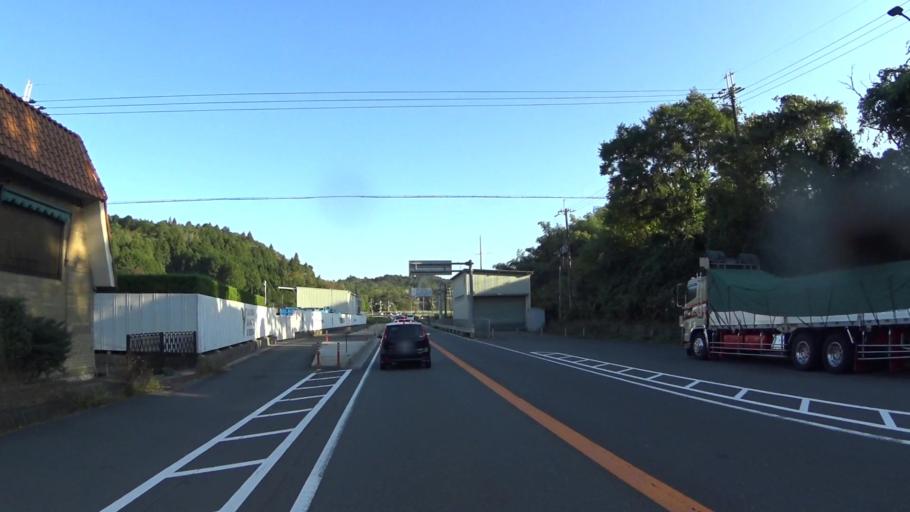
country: JP
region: Kyoto
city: Ayabe
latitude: 35.1819
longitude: 135.3456
